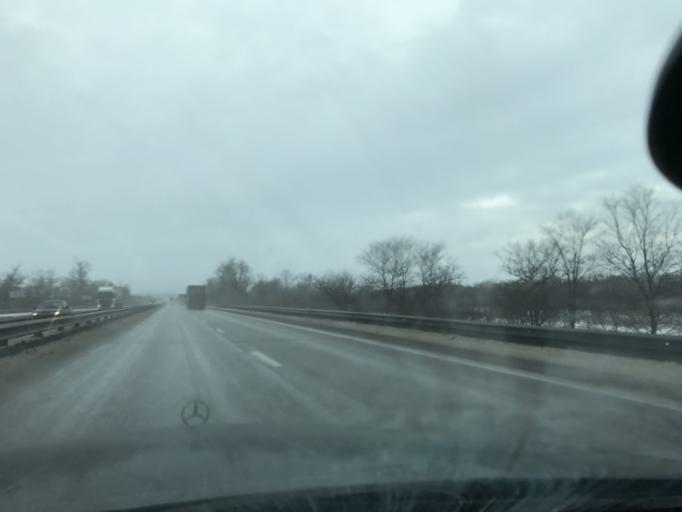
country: RU
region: Vladimir
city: Gorokhovets
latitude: 56.2157
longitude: 42.7578
